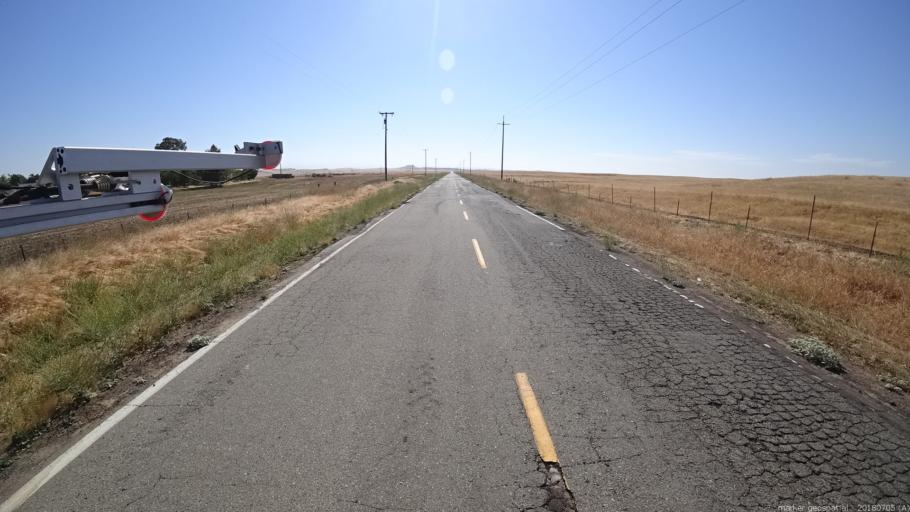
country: US
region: California
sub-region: Madera County
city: Madera Acres
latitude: 37.1268
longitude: -120.0410
